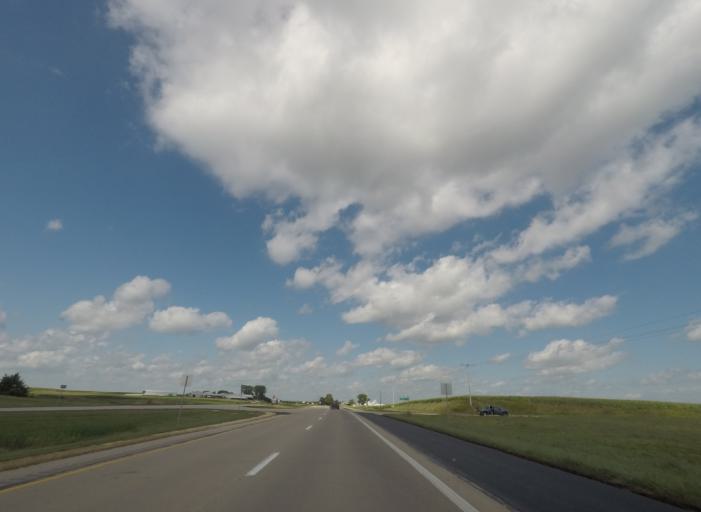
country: US
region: Iowa
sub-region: Jones County
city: Monticello
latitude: 42.2670
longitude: -91.1442
